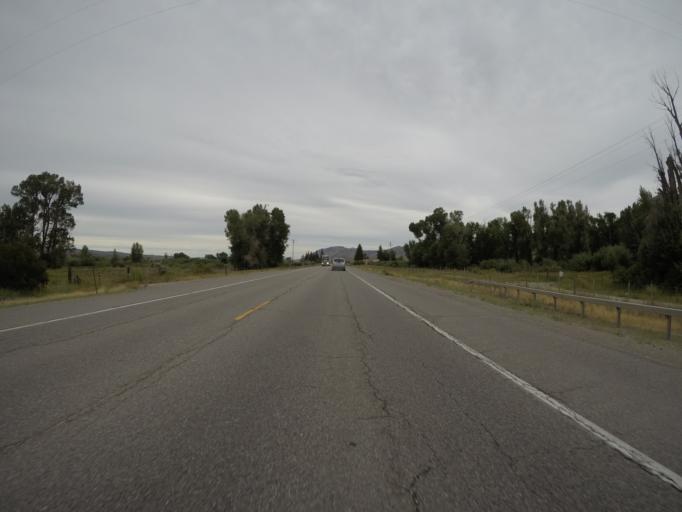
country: US
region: Idaho
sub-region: Bear Lake County
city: Montpelier
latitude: 42.0929
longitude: -110.9507
